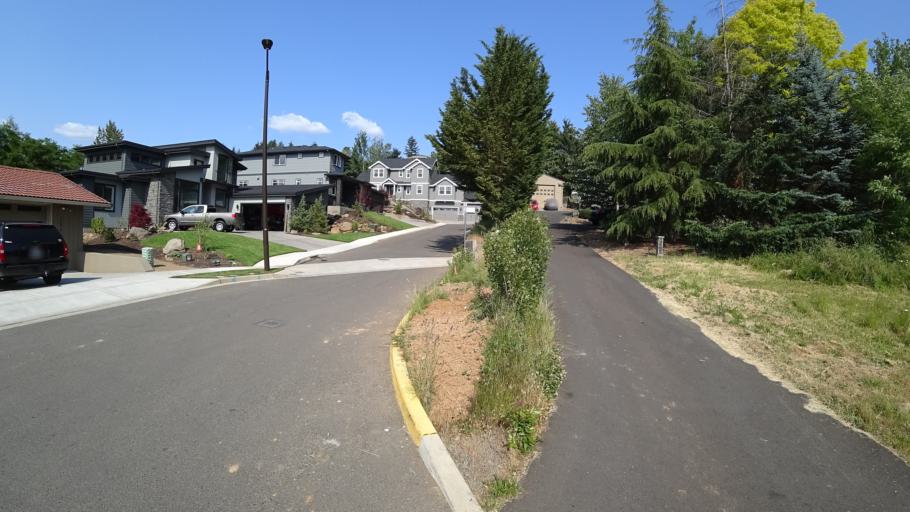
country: US
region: Oregon
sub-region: Clackamas County
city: Sunnyside
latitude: 45.4359
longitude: -122.5347
